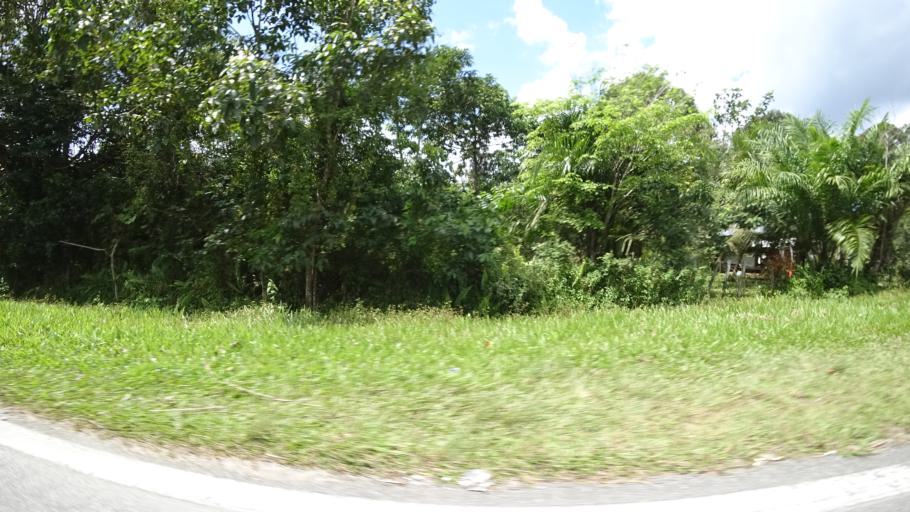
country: BN
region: Tutong
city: Tutong
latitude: 4.6919
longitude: 114.8047
